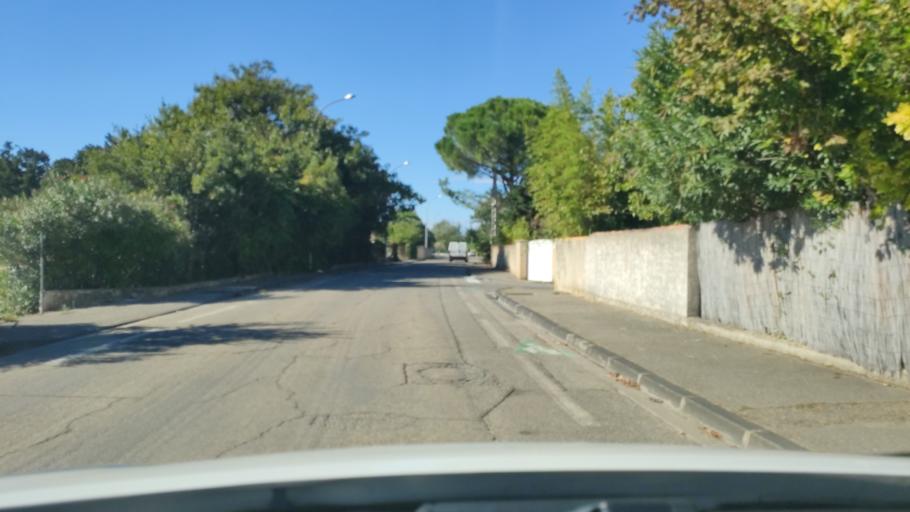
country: FR
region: Provence-Alpes-Cote d'Azur
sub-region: Departement du Vaucluse
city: Morieres-les-Avignon
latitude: 43.9442
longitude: 4.8992
